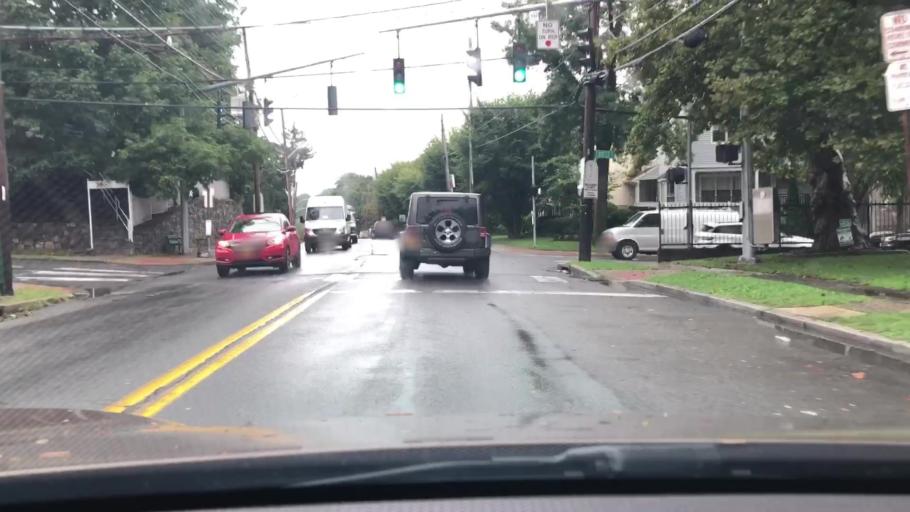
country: US
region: New York
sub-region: Westchester County
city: Tuckahoe
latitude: 40.9504
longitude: -73.8383
